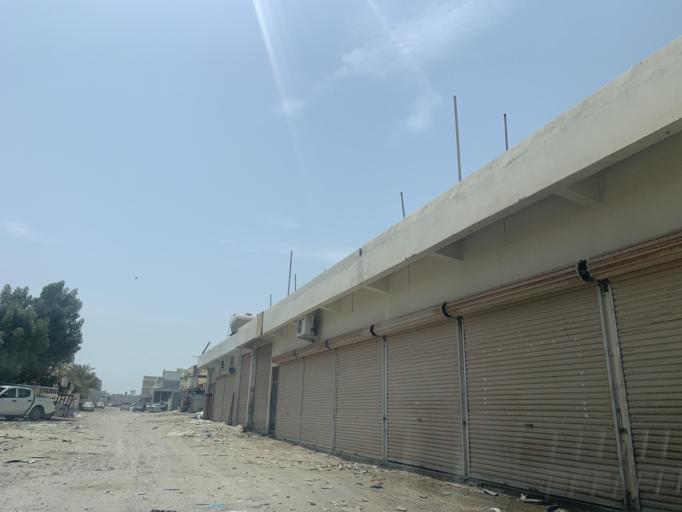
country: BH
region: Central Governorate
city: Madinat Hamad
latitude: 26.1437
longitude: 50.4864
